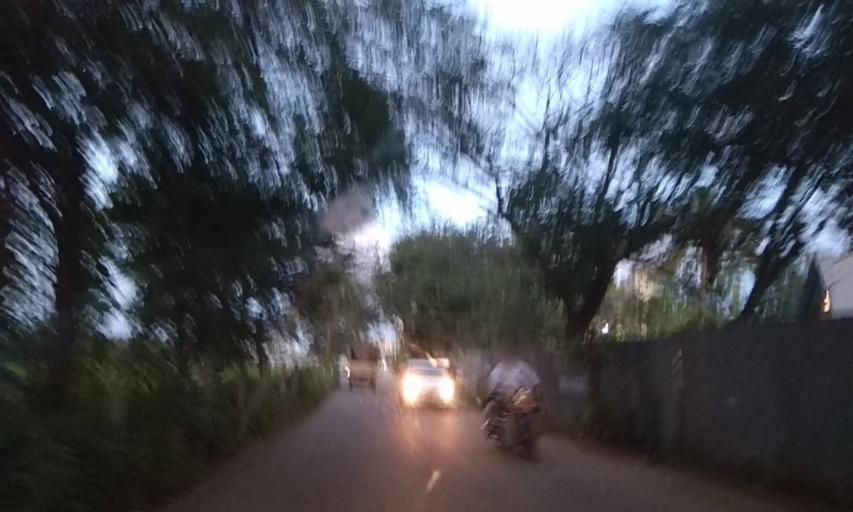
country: IN
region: Maharashtra
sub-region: Pune Division
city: Pune
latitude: 18.5202
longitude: 73.9192
